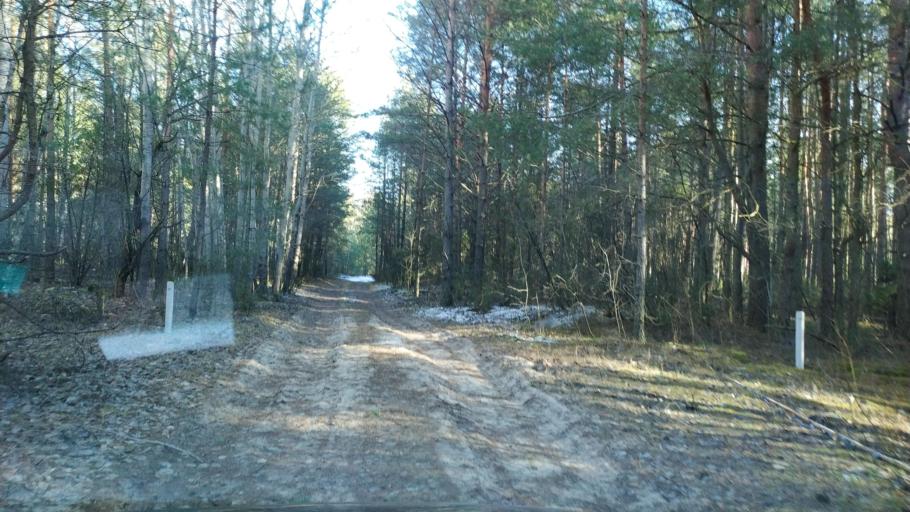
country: BY
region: Brest
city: Zhabinka
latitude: 52.4512
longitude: 24.1420
